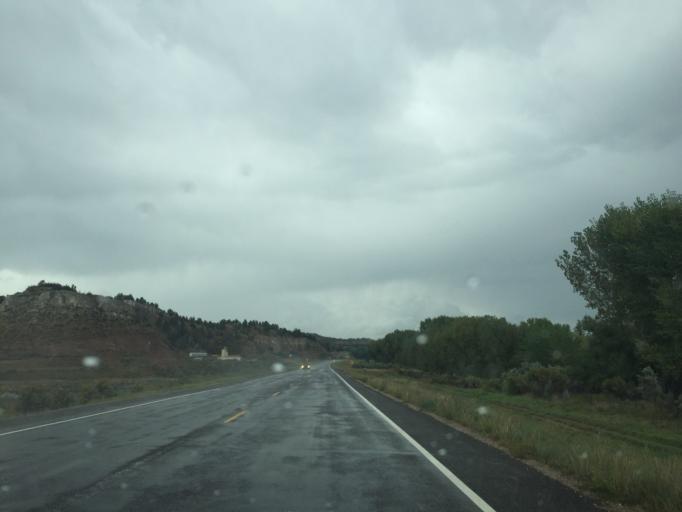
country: US
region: Utah
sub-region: Kane County
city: Kanab
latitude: 37.2335
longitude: -112.6754
